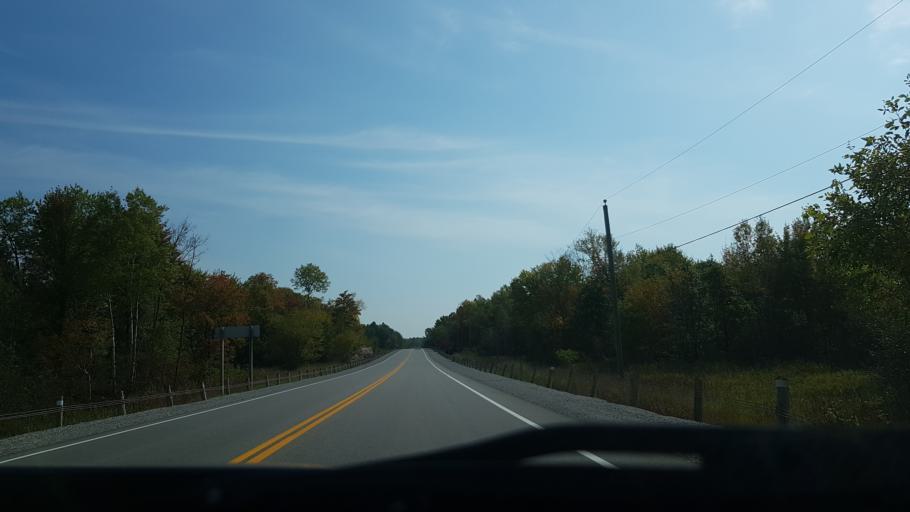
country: CA
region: Ontario
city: Orillia
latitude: 44.7424
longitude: -79.3079
